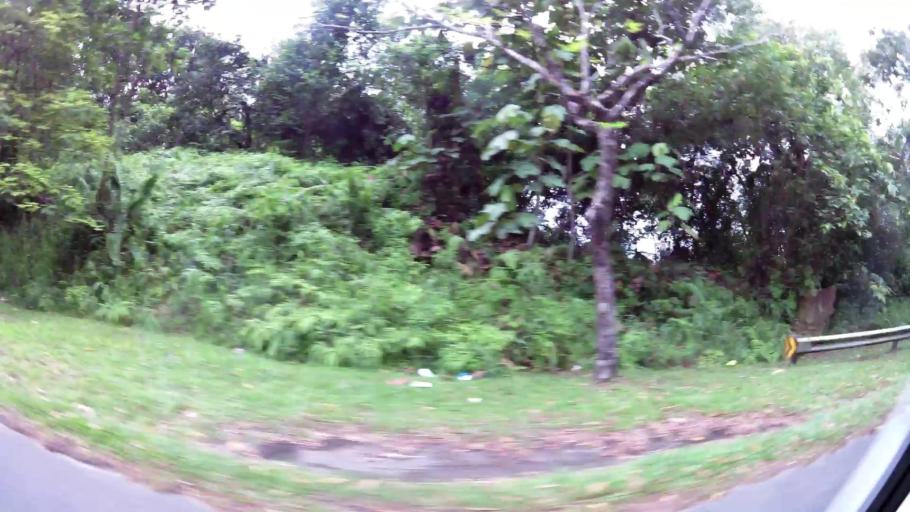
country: BN
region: Brunei and Muara
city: Bandar Seri Begawan
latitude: 4.8794
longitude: 114.8945
